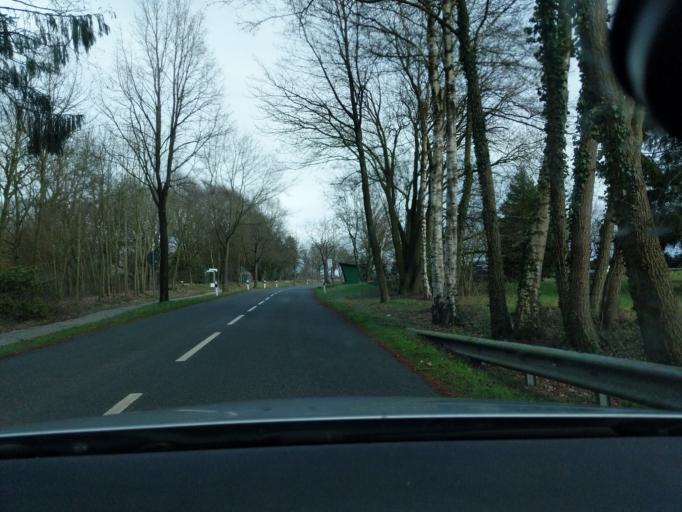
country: DE
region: Lower Saxony
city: Heinbockel
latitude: 53.5813
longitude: 9.2969
